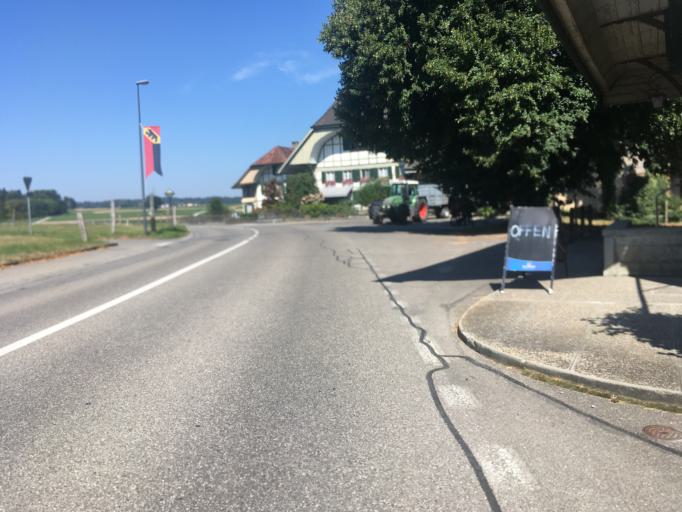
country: CH
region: Bern
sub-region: Bern-Mittelland District
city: Fraubrunnen
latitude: 47.0746
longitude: 7.5381
